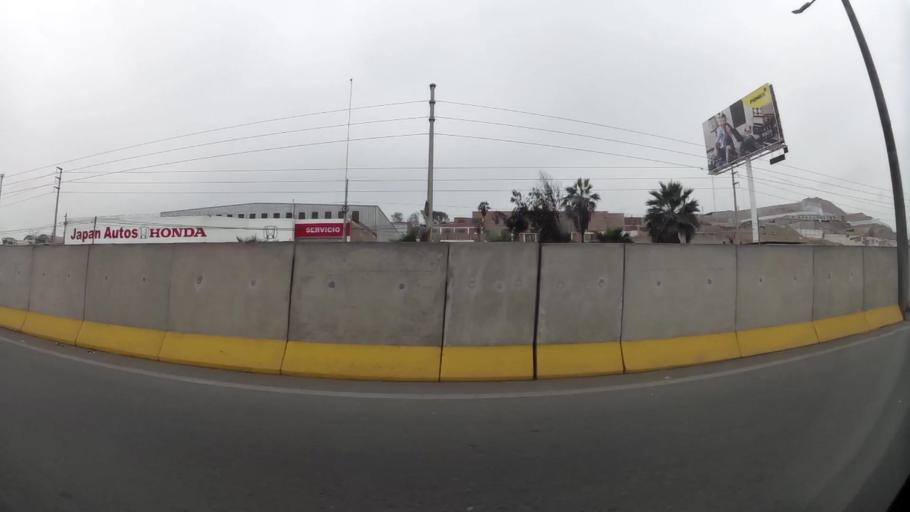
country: PE
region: Lima
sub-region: Lima
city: Surco
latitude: -12.2281
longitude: -76.9692
